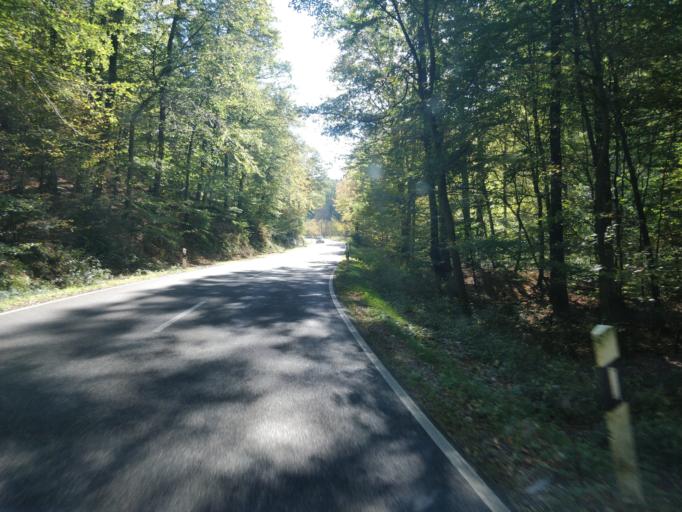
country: DE
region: North Rhine-Westphalia
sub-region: Regierungsbezirk Koln
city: Bad Munstereifel
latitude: 50.5549
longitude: 6.7992
